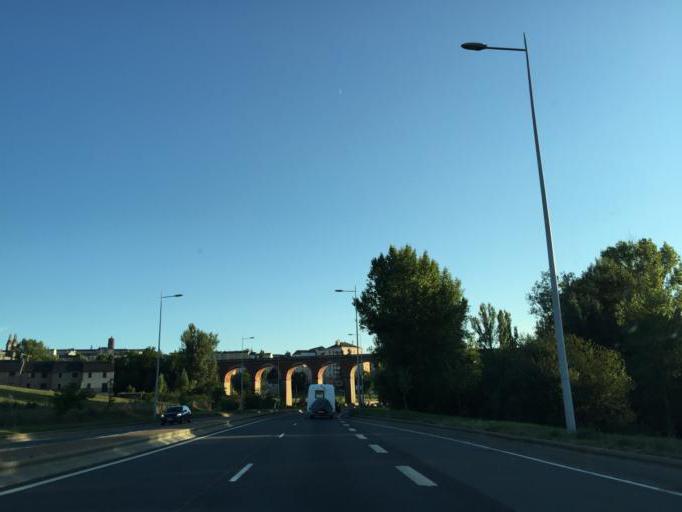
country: FR
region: Midi-Pyrenees
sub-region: Departement de l'Aveyron
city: Rodez
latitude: 44.3657
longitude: 2.5778
